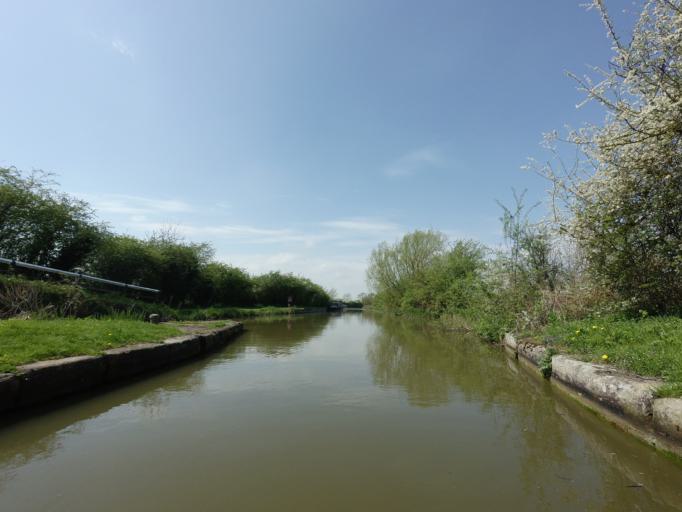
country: GB
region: England
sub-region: Buckinghamshire
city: Cheddington
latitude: 51.8734
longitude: -0.6527
